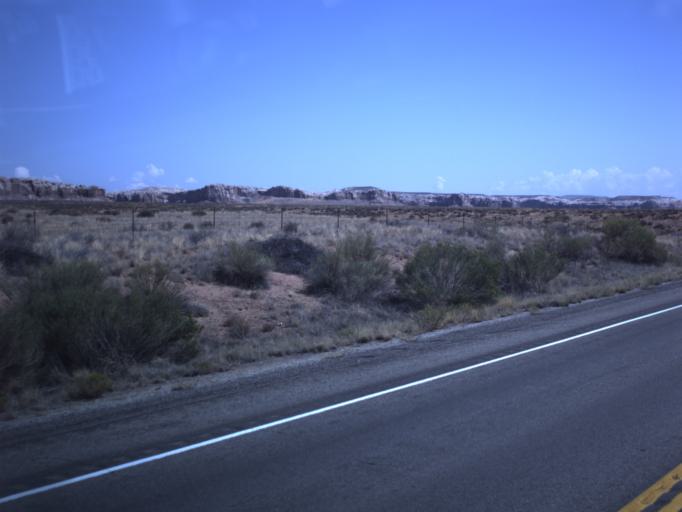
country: US
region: Utah
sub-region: San Juan County
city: Blanding
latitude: 37.2670
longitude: -109.6100
